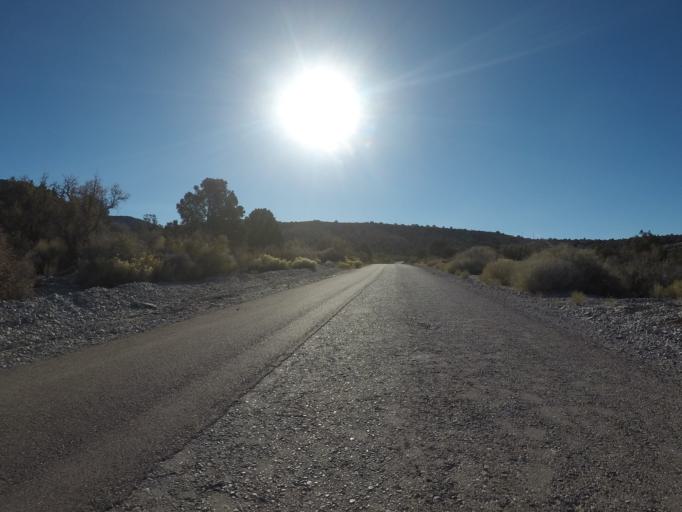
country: US
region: Nevada
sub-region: Clark County
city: Summerlin South
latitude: 36.0883
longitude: -115.5605
